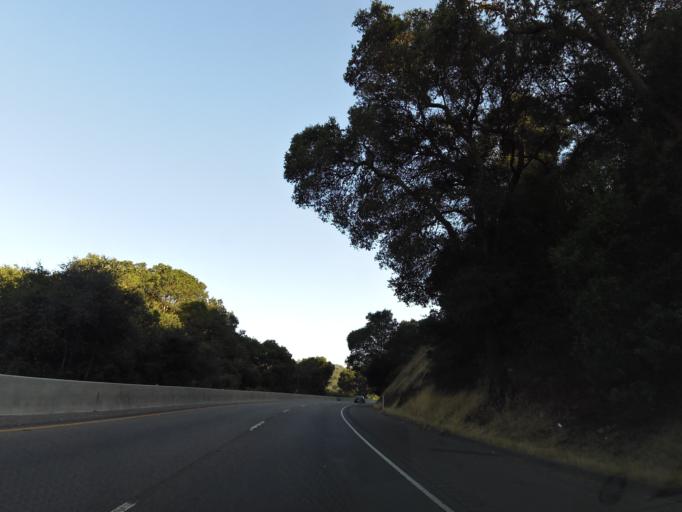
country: US
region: California
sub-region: San Luis Obispo County
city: Santa Margarita
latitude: 35.3654
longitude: -120.6393
